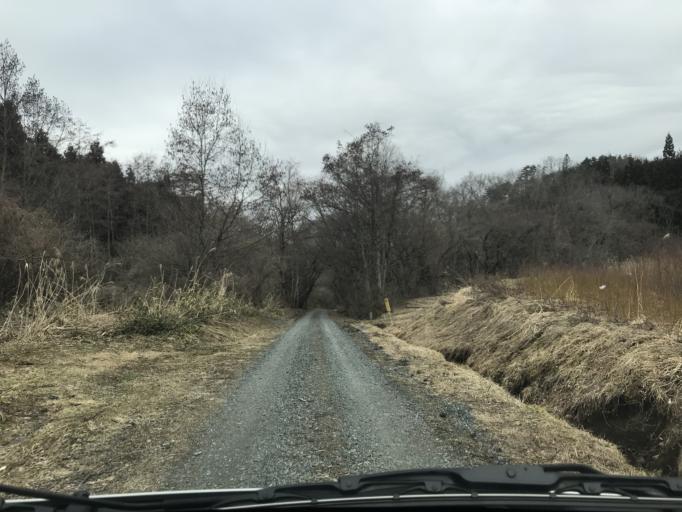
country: JP
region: Iwate
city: Kitakami
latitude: 39.3142
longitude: 141.2268
